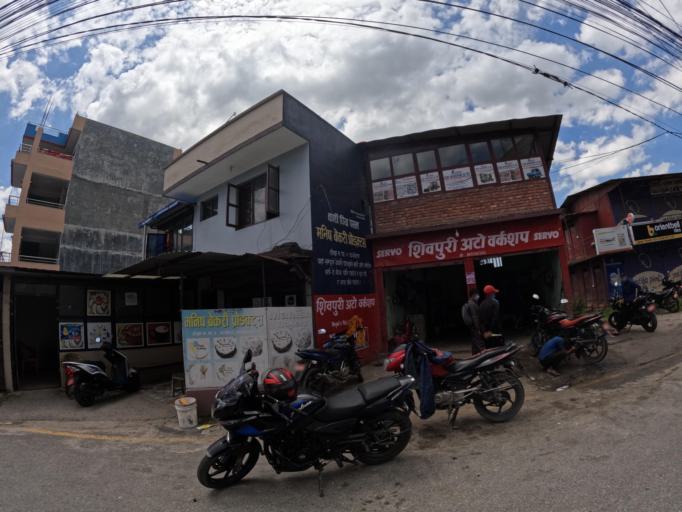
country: NP
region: Central Region
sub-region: Bagmati Zone
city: Kathmandu
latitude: 27.7789
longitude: 85.3255
